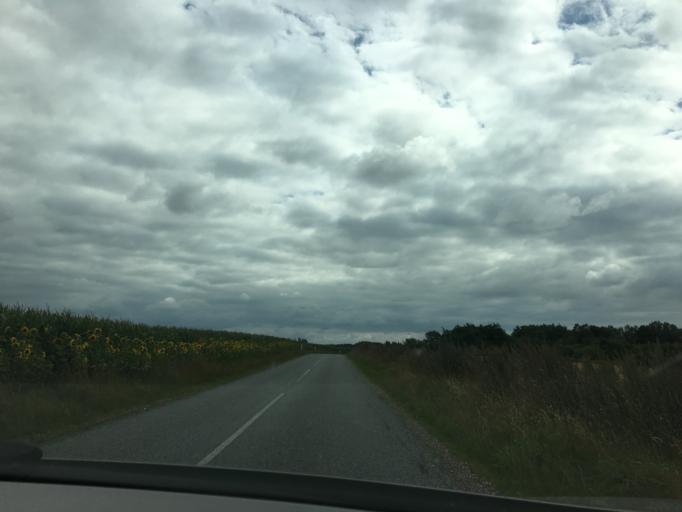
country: DK
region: Central Jutland
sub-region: Ringkobing-Skjern Kommune
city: Videbaek
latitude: 56.0819
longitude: 8.6554
